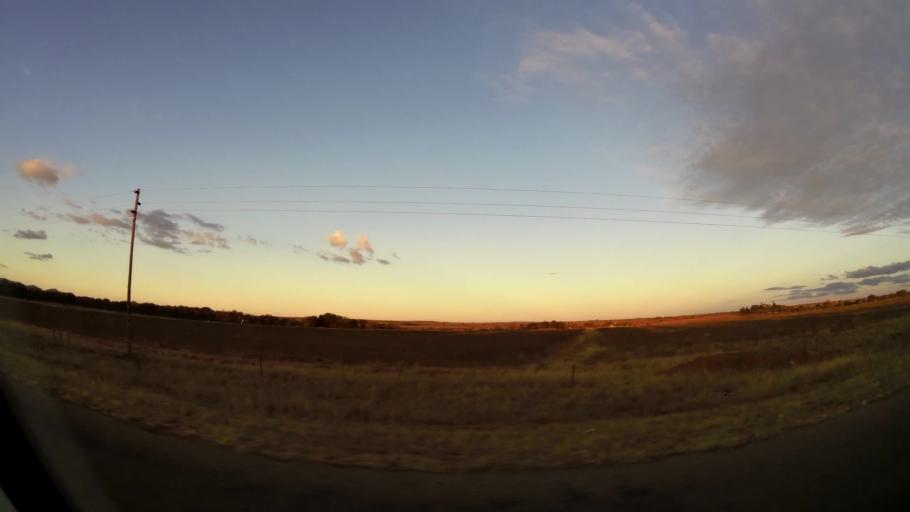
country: ZA
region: Limpopo
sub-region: Capricorn District Municipality
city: Polokwane
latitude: -23.7730
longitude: 29.4737
